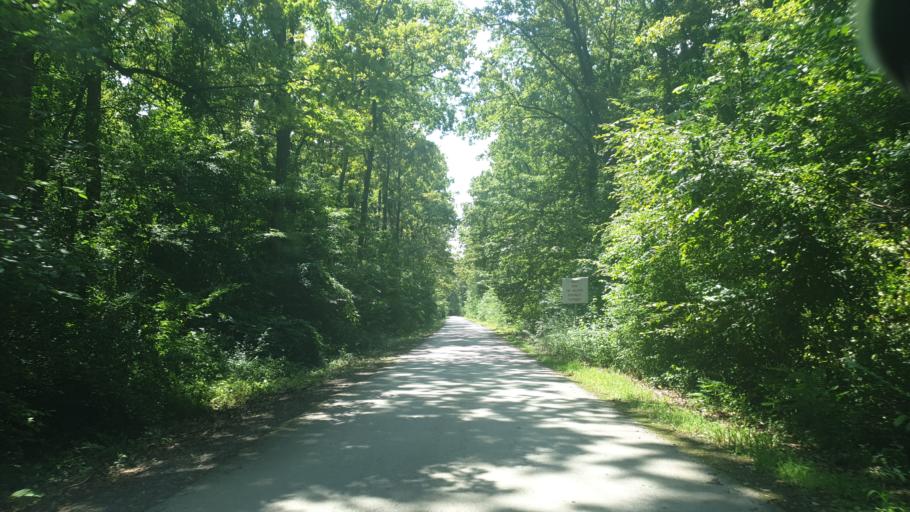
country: RS
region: Autonomna Pokrajina Vojvodina
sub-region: Sremski Okrug
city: Sid
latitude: 45.0406
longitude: 19.1384
